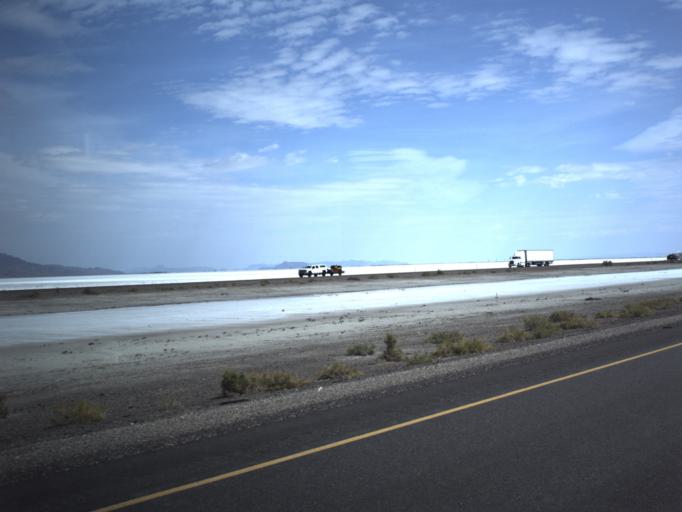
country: US
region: Utah
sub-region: Tooele County
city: Wendover
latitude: 40.7399
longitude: -113.9240
